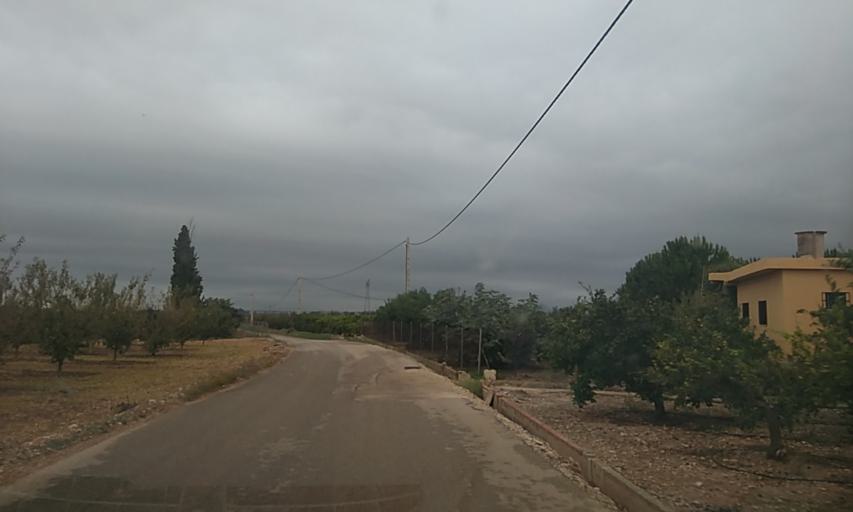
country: ES
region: Valencia
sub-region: Provincia de Valencia
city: Benimodo
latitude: 39.1882
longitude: -0.5460
